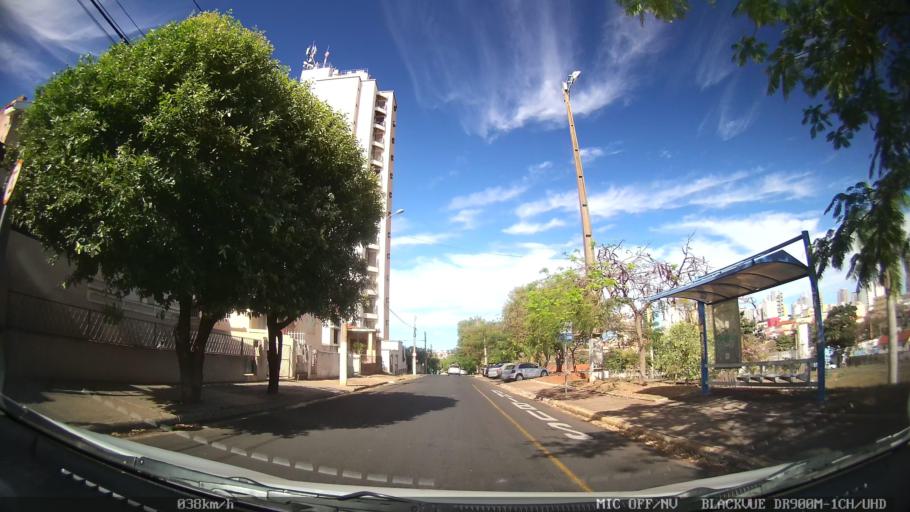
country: BR
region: Sao Paulo
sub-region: Catanduva
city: Catanduva
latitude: -21.1341
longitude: -48.9671
